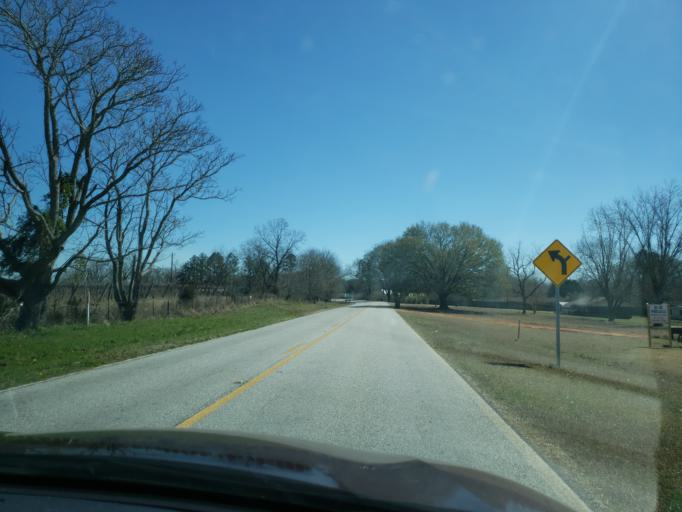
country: US
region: Alabama
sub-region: Elmore County
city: Tallassee
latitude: 32.5831
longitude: -85.7913
